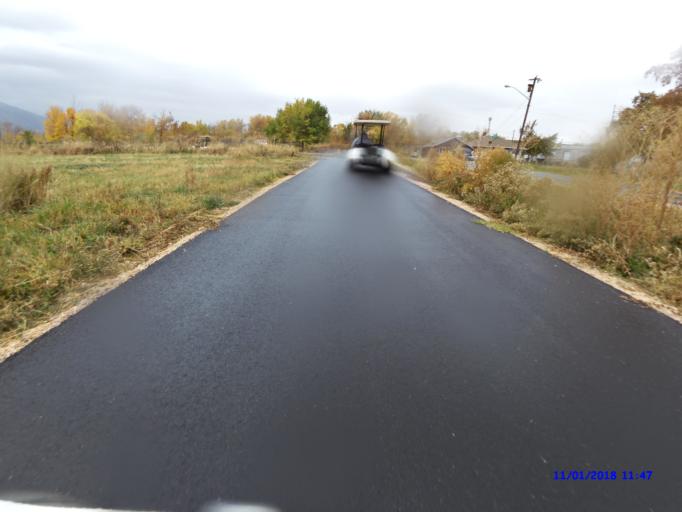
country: US
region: Utah
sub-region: Weber County
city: Ogden
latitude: 41.2339
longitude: -111.9859
